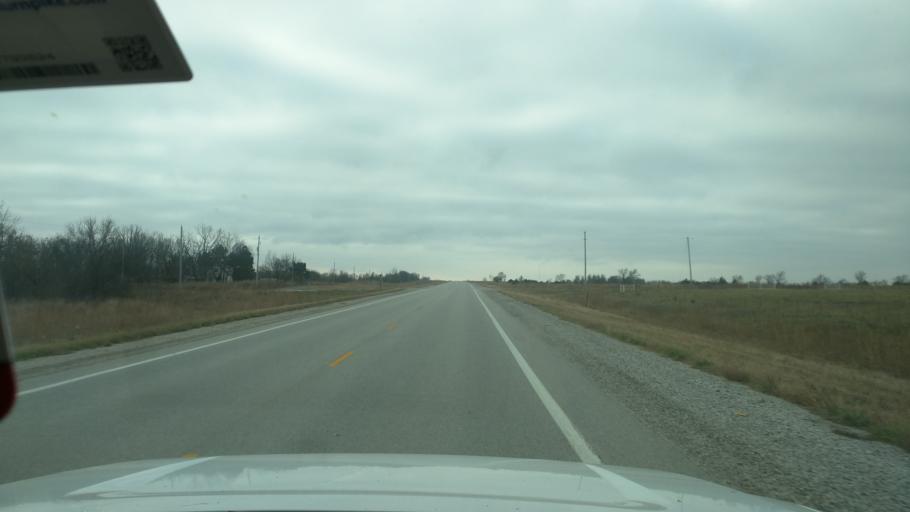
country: US
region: Kansas
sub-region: Elk County
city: Howard
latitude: 37.5783
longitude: -96.2534
